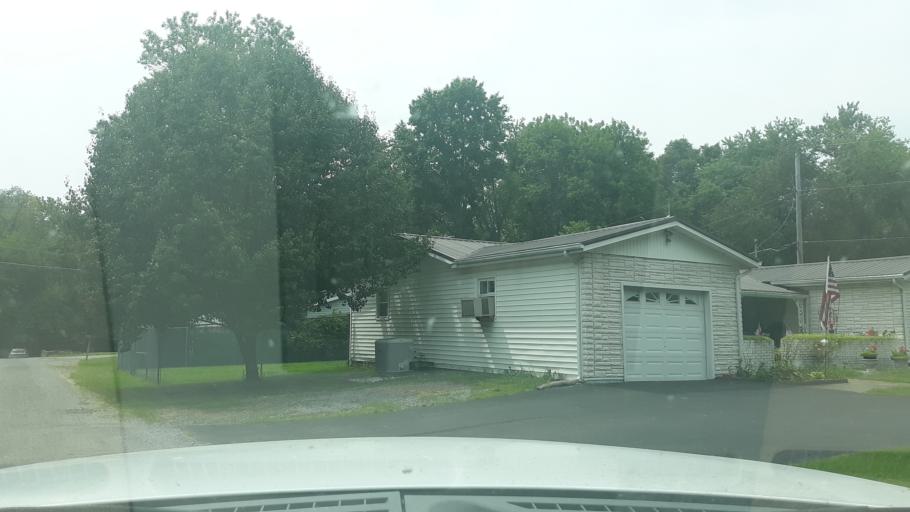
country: US
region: Illinois
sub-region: Saline County
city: Harrisburg
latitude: 37.8451
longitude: -88.6100
